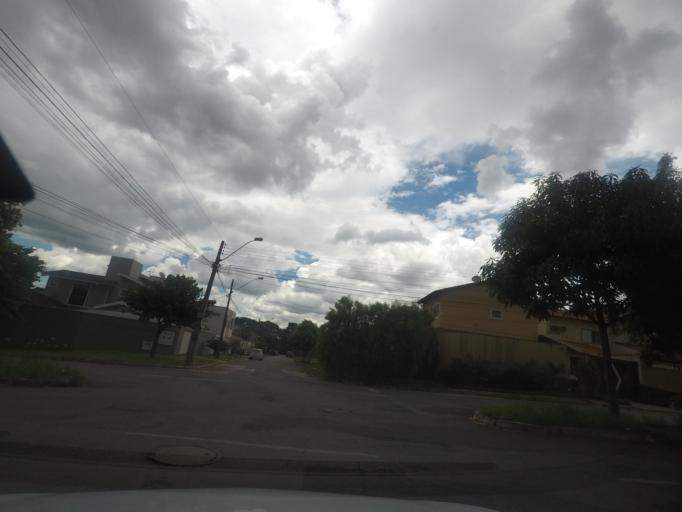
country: BR
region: Goias
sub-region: Goiania
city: Goiania
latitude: -16.6407
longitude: -49.2244
